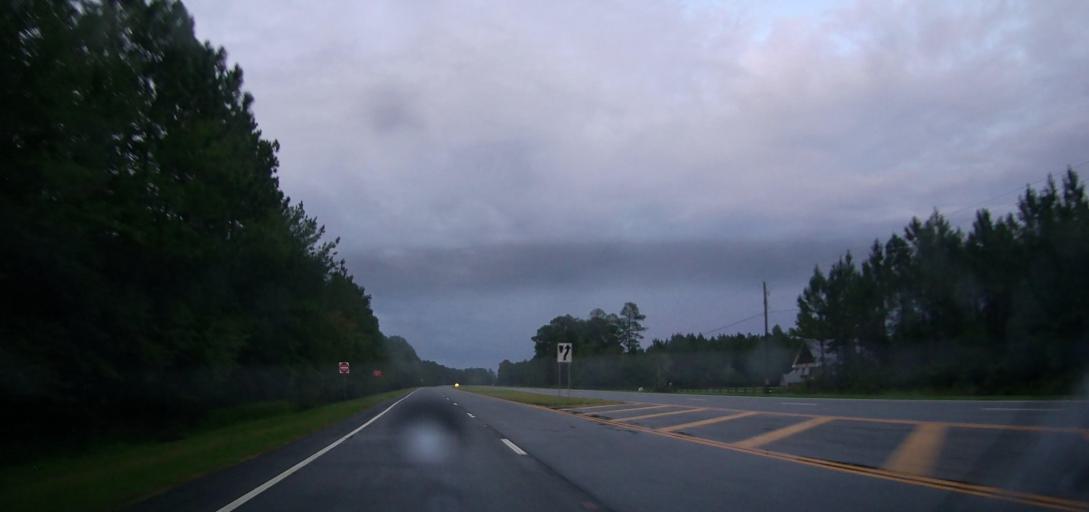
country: US
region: Georgia
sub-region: Lanier County
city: Lakeland
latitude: 30.9126
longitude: -83.0694
